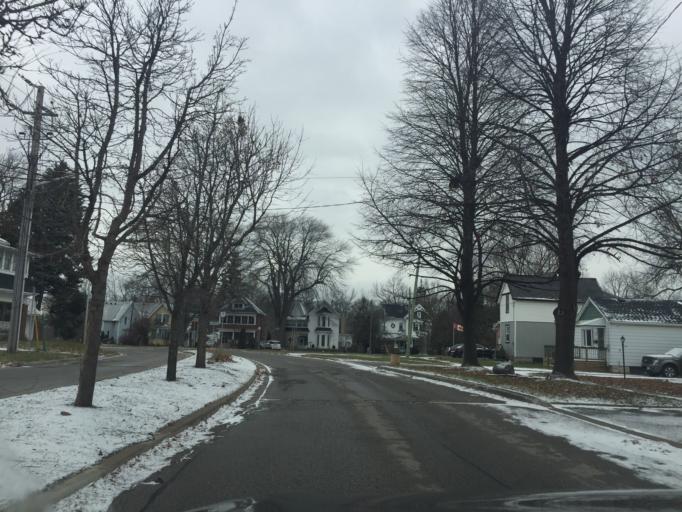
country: CA
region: Ontario
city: St. Thomas
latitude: 42.7700
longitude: -81.1961
